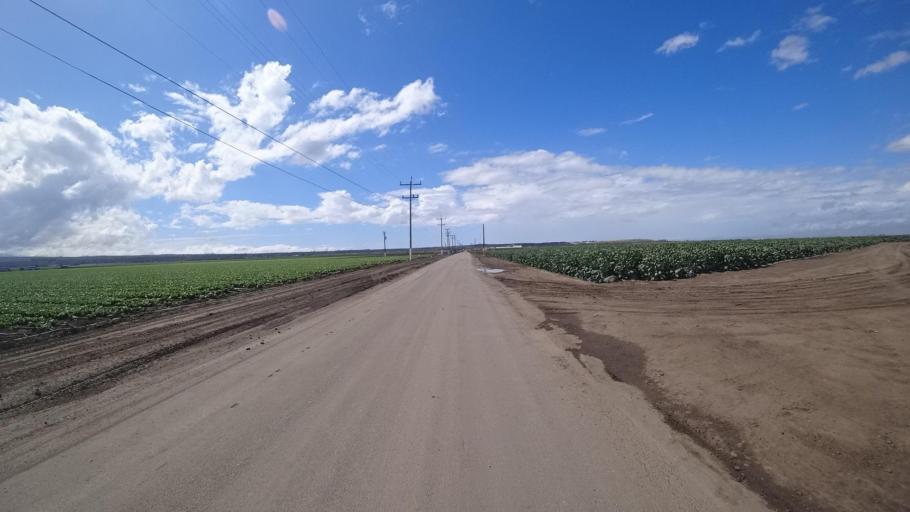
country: US
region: California
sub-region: Monterey County
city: Boronda
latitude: 36.6902
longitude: -121.7212
